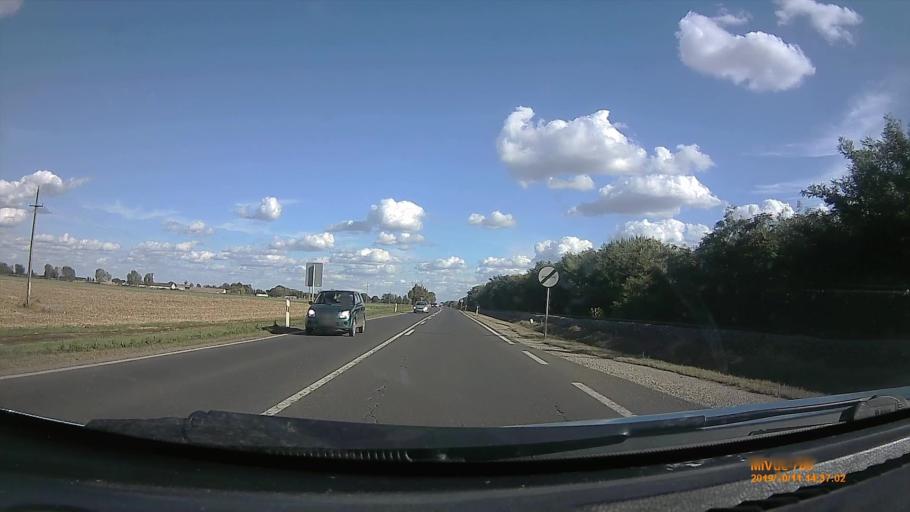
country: HU
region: Hajdu-Bihar
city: Ebes
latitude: 47.5552
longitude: 21.5187
